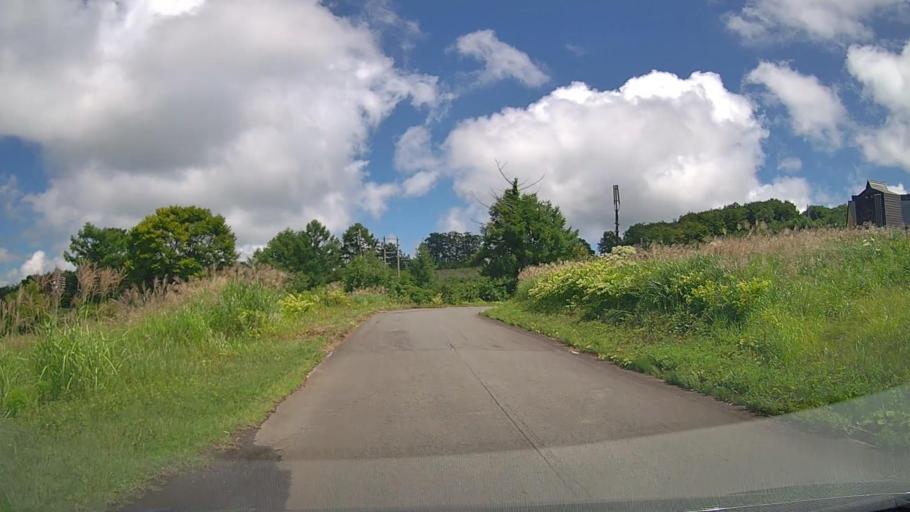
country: JP
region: Nagano
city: Iiyama
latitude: 36.9226
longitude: 138.4769
